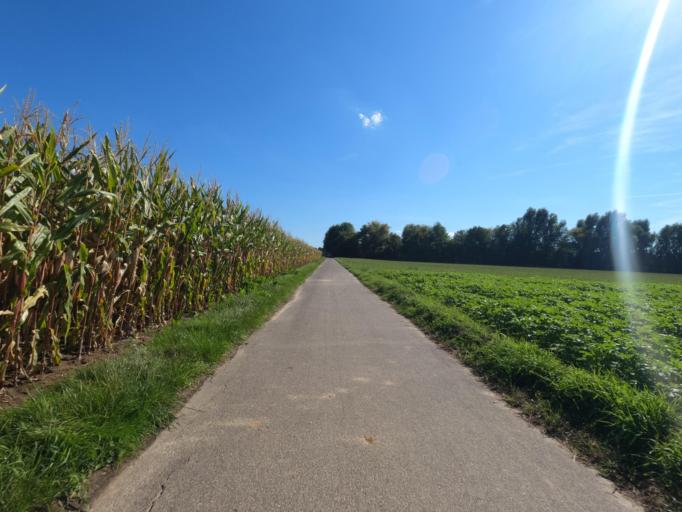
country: DE
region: North Rhine-Westphalia
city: Baesweiler
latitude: 50.8919
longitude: 6.1995
